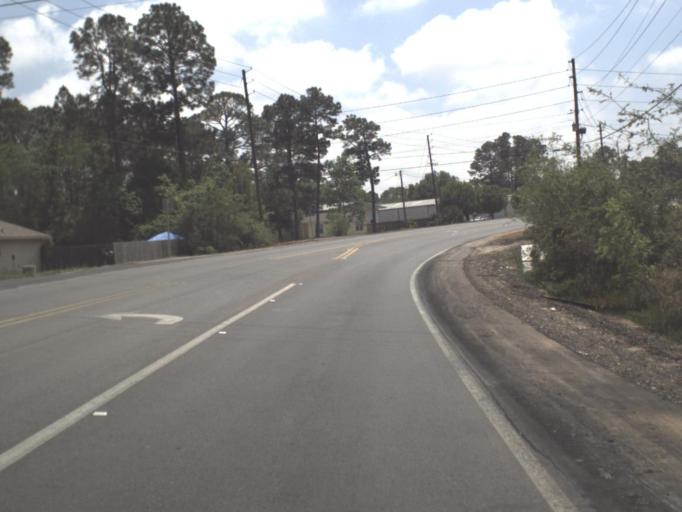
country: US
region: Florida
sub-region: Escambia County
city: Myrtle Grove
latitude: 30.3892
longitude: -87.3084
